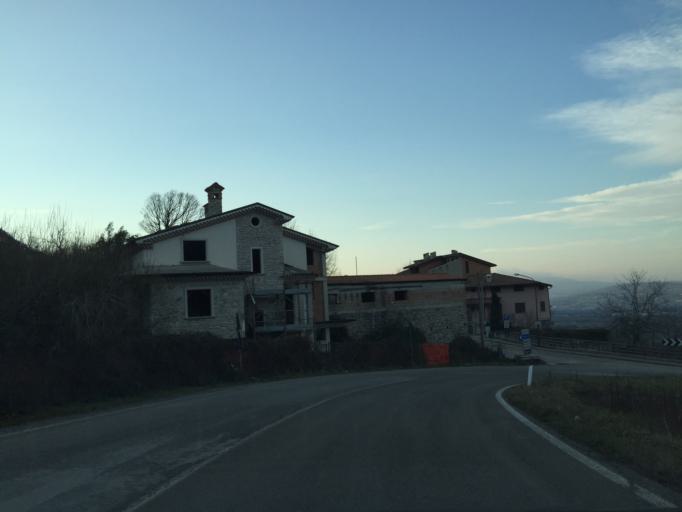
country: IT
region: Molise
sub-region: Provincia di Campobasso
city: Guardiaregia
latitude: 41.4353
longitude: 14.5446
